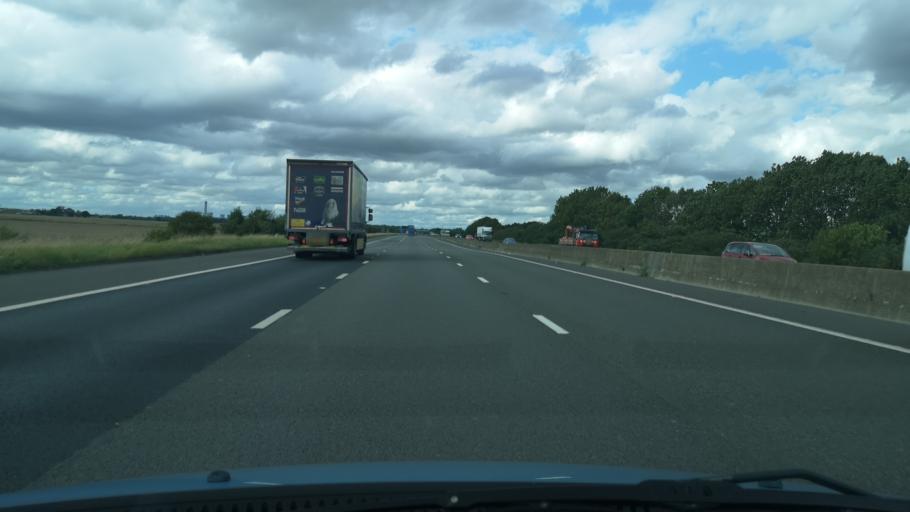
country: GB
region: England
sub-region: East Riding of Yorkshire
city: Rawcliffe
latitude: 53.6589
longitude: -0.9651
